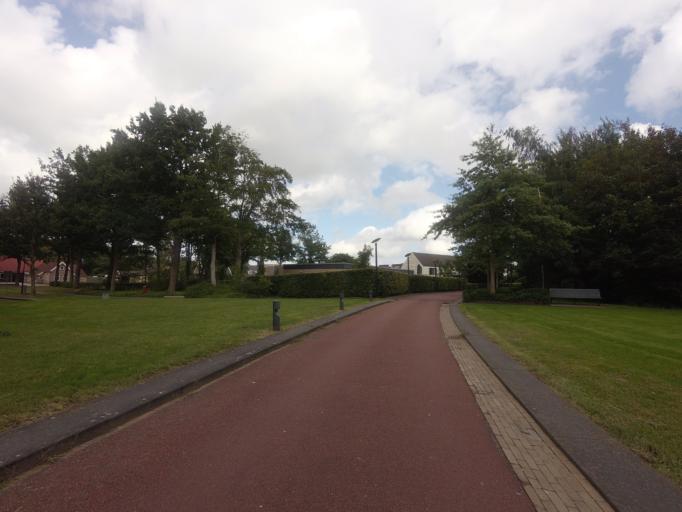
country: NL
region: Friesland
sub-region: Gemeente Heerenveen
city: Jubbega
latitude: 52.9947
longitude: 6.2941
